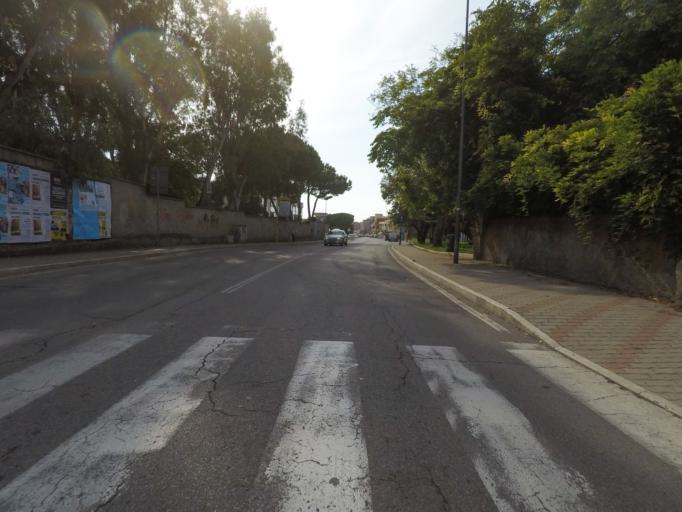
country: IT
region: Latium
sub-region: Citta metropolitana di Roma Capitale
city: Civitavecchia
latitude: 42.0984
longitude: 11.7987
